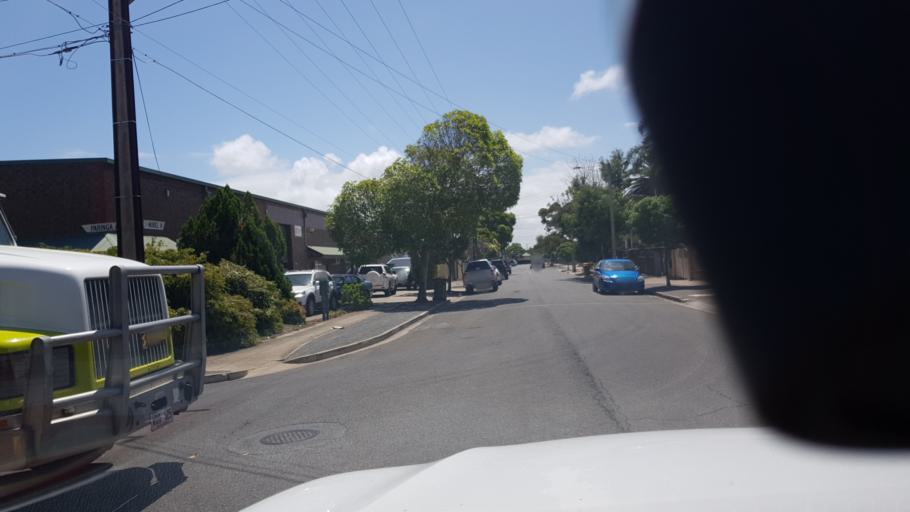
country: AU
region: South Australia
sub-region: Holdfast Bay
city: North Brighton
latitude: -34.9990
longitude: 138.5295
